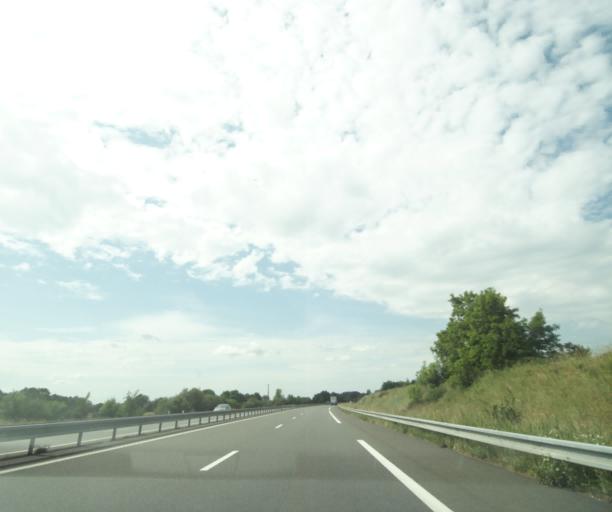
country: FR
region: Pays de la Loire
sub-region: Departement de Maine-et-Loire
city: Jumelles
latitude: 47.3975
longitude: -0.1150
